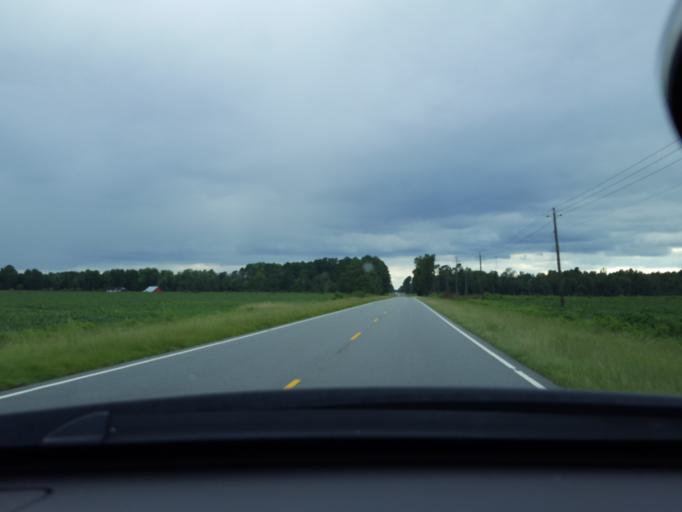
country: US
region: North Carolina
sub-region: Bladen County
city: Elizabethtown
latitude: 34.7459
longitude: -78.4237
